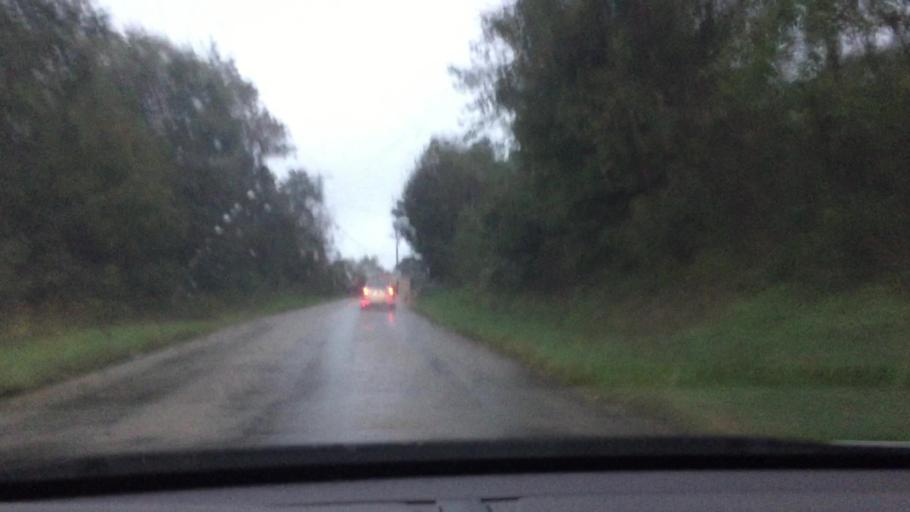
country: US
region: Pennsylvania
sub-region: Washington County
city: Bentleyville
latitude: 40.1299
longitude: -79.9720
